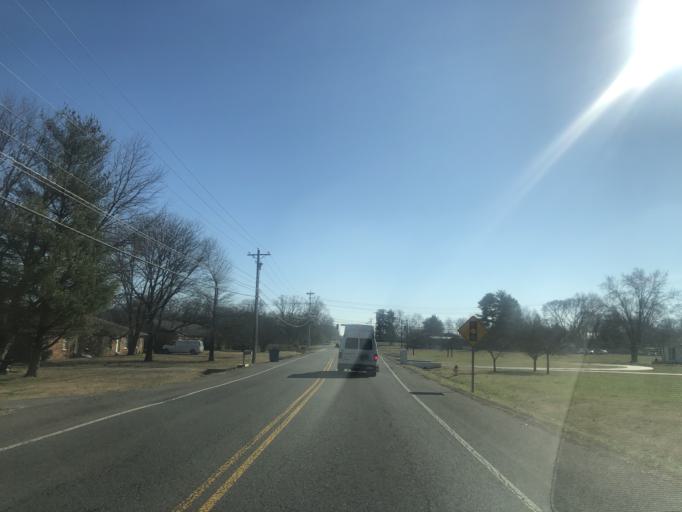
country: US
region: Tennessee
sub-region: Rutherford County
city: Smyrna
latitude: 35.9148
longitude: -86.4712
